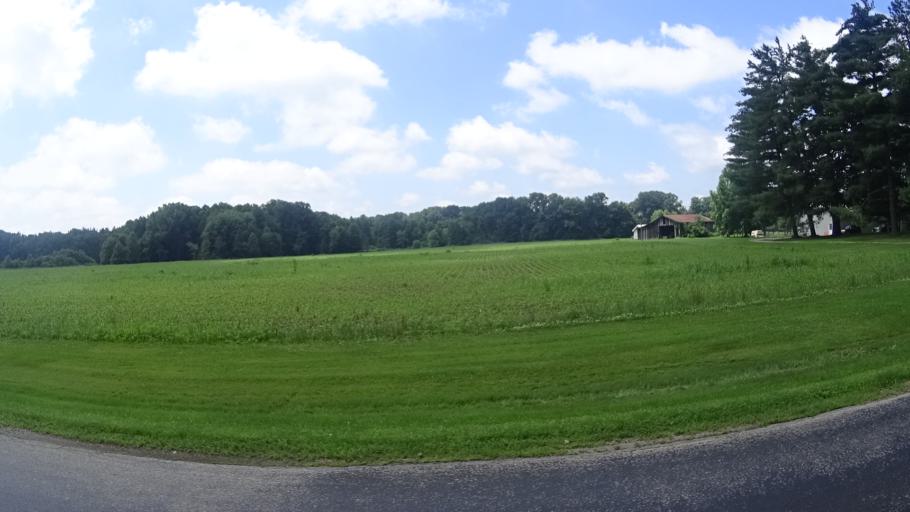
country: US
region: Ohio
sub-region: Huron County
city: Wakeman
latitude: 41.3205
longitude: -82.3561
